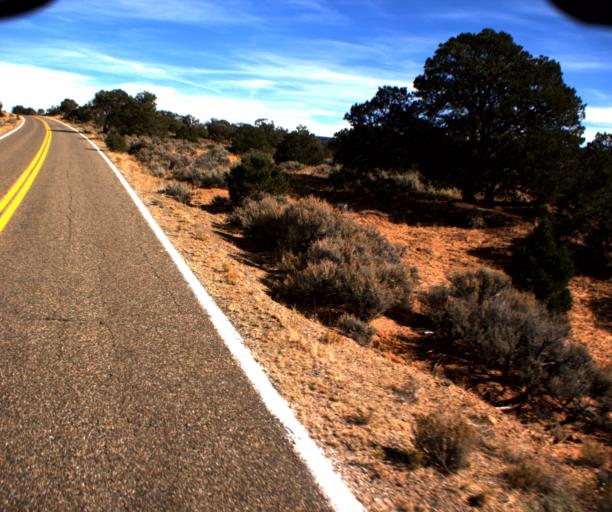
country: US
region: Arizona
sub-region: Navajo County
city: Kayenta
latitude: 36.5741
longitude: -110.4941
